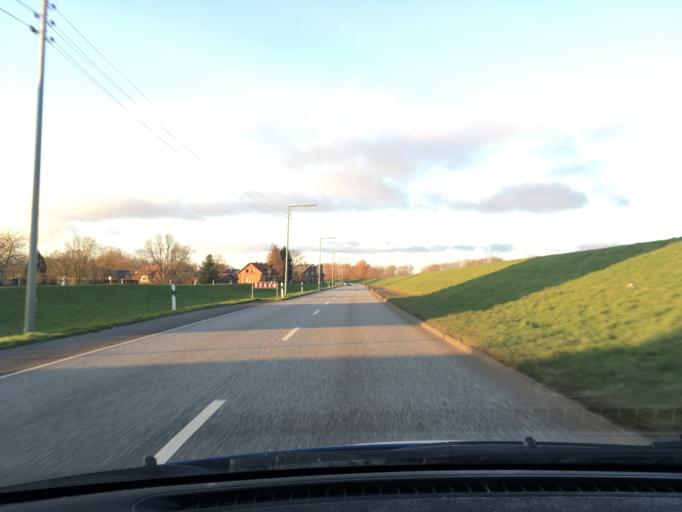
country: DE
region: Hamburg
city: Harburg
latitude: 53.4638
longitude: 10.0489
